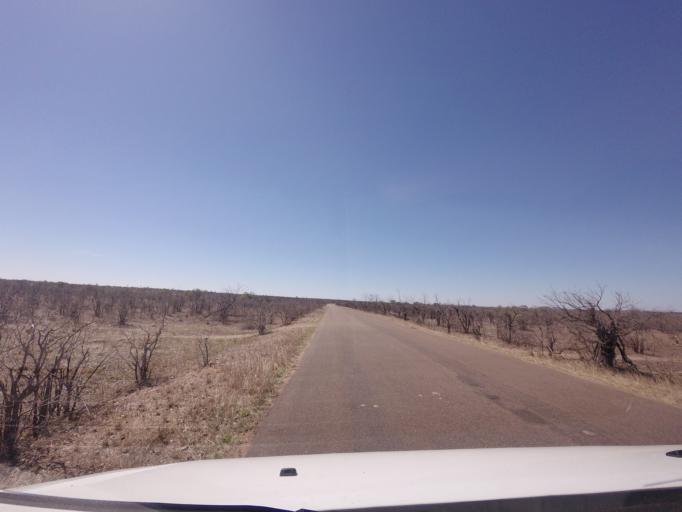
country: ZA
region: Limpopo
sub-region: Mopani District Municipality
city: Giyani
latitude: -23.2434
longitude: 31.3157
